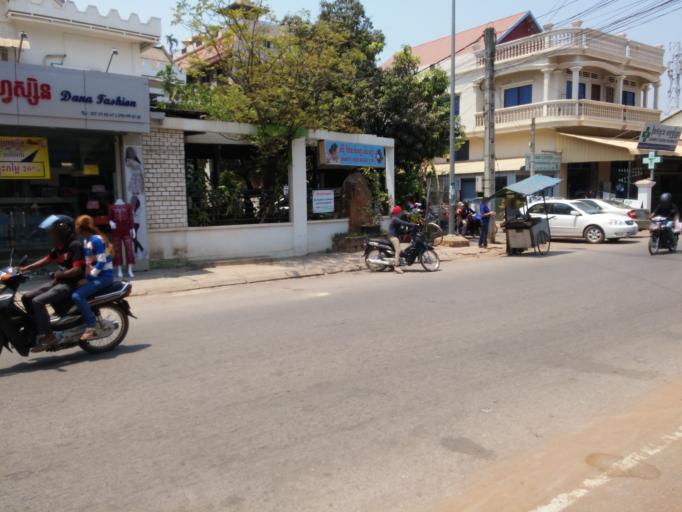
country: KH
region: Siem Reap
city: Siem Reap
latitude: 13.3552
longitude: 103.8595
